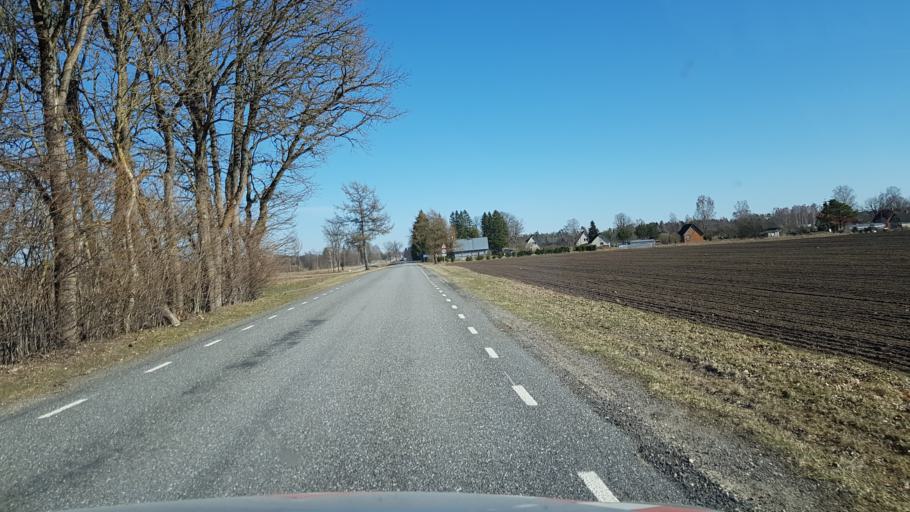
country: EE
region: Laeaene-Virumaa
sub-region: Rakke vald
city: Rakke
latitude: 59.0006
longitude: 26.1986
